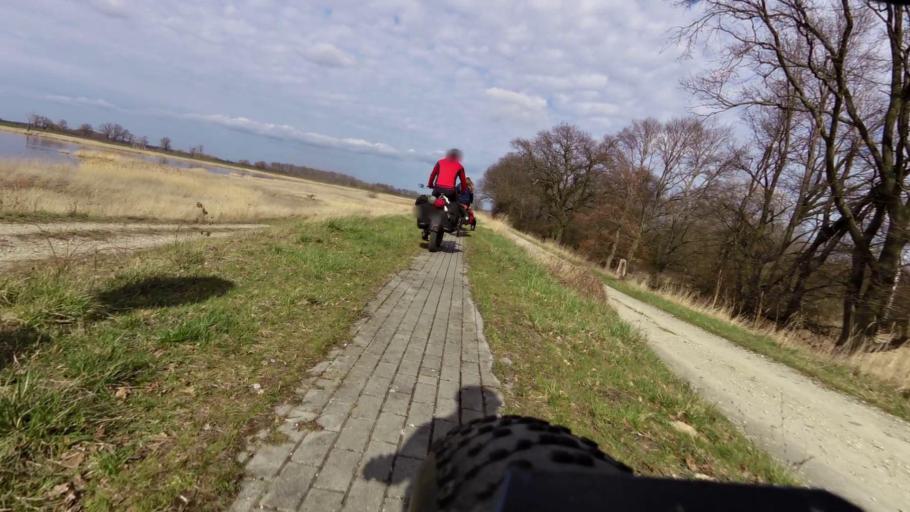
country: DE
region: Brandenburg
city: Reitwein
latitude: 52.4736
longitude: 14.6141
